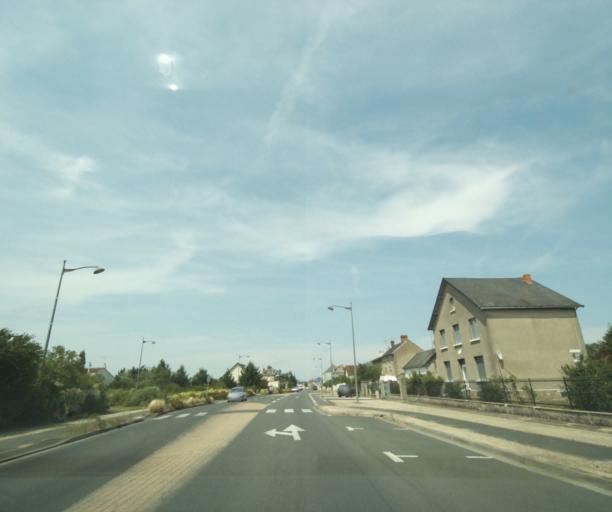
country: FR
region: Poitou-Charentes
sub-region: Departement de la Vienne
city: Dange-Saint-Romain
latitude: 46.9312
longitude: 0.6046
